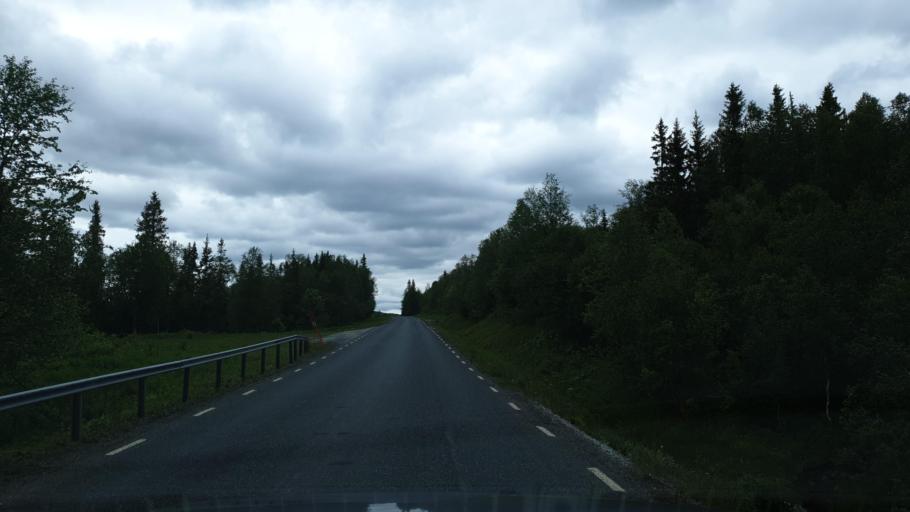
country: SE
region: Vaesterbotten
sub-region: Vilhelmina Kommun
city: Sjoberg
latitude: 65.2810
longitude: 15.3022
